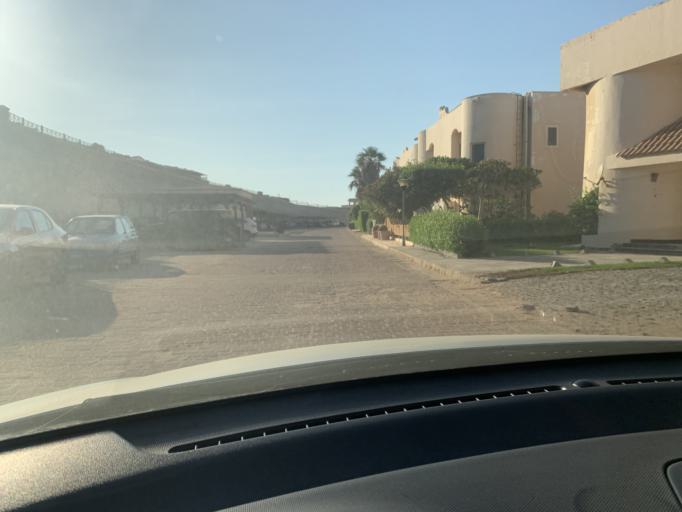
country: EG
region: As Suways
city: Ain Sukhna
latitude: 29.3743
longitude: 32.5713
